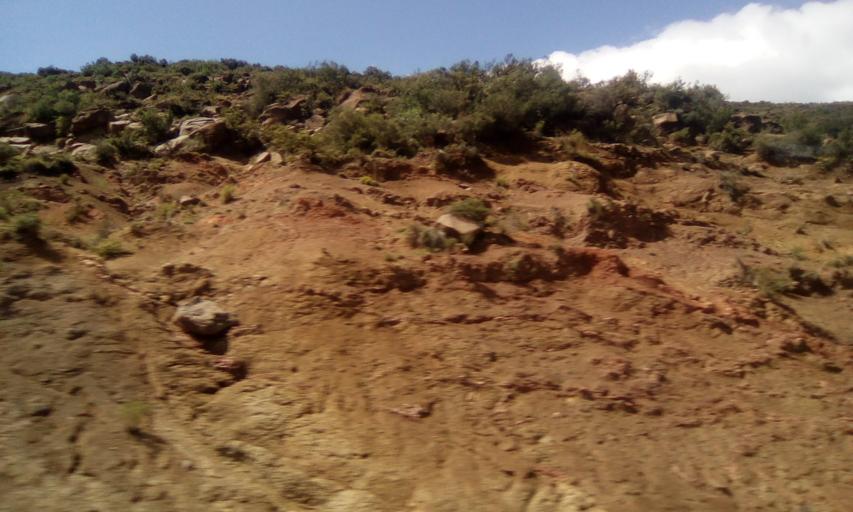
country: LS
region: Maseru
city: Nako
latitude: -29.6563
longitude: 27.8396
